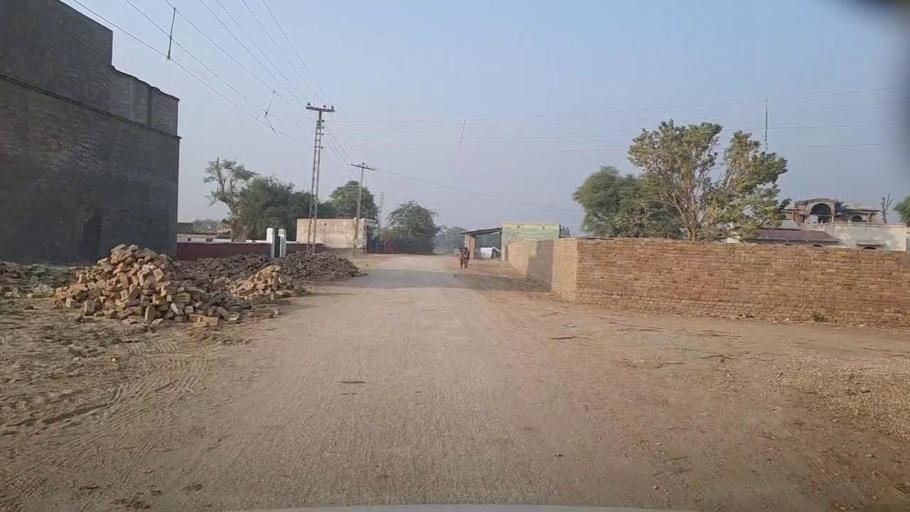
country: PK
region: Sindh
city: Kandiari
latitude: 27.0071
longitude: 68.4620
